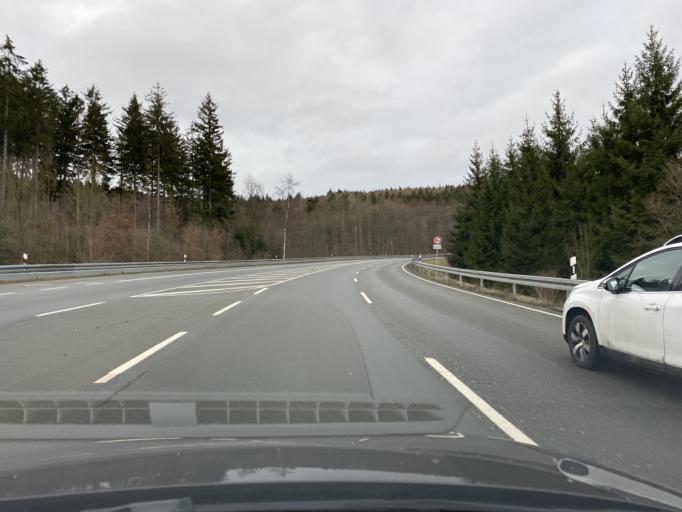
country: DE
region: North Rhine-Westphalia
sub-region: Regierungsbezirk Arnsberg
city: Meschede
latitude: 51.3734
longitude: 8.2923
